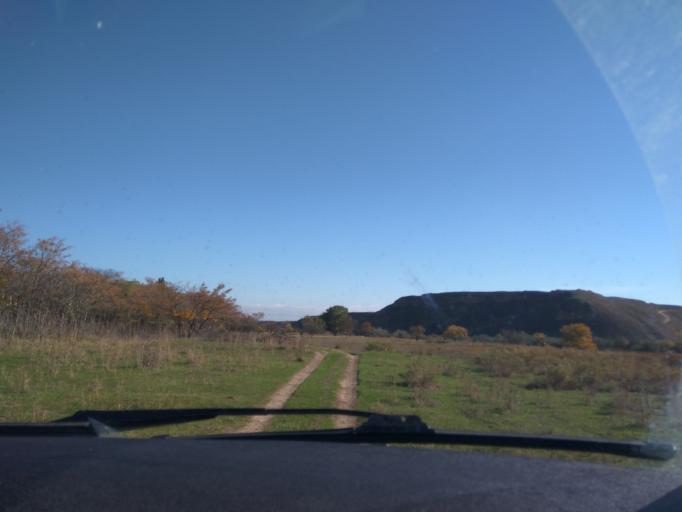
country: RU
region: Dagestan
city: Korkmaskala
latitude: 43.0002
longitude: 47.2333
